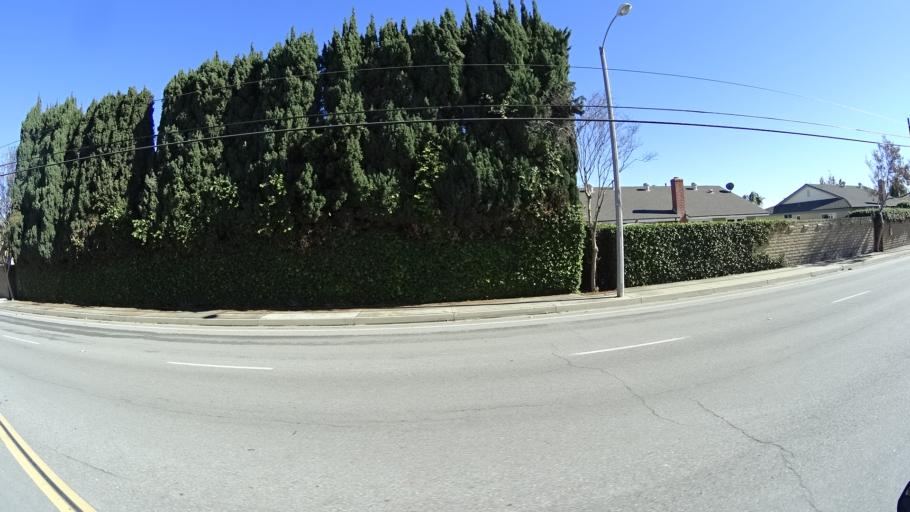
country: US
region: California
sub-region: Orange County
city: Placentia
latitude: 33.8990
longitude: -117.8550
